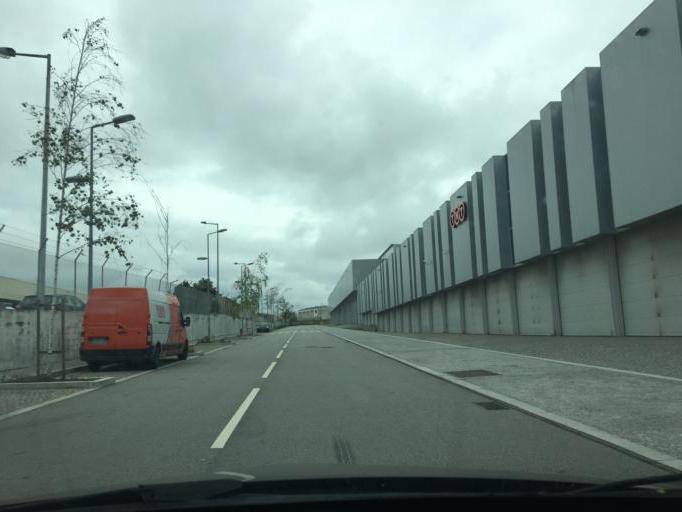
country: PT
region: Porto
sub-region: Matosinhos
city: Santa Cruz do Bispo
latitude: 41.2328
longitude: -8.6645
